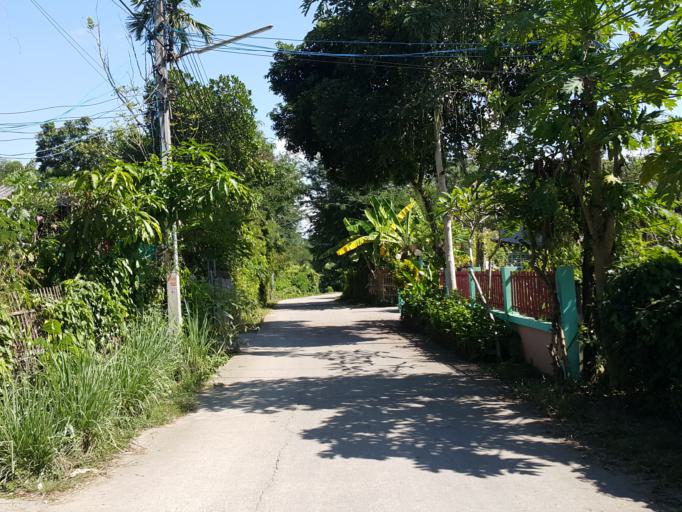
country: TH
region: Chiang Mai
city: San Kamphaeng
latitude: 18.7769
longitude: 99.1159
